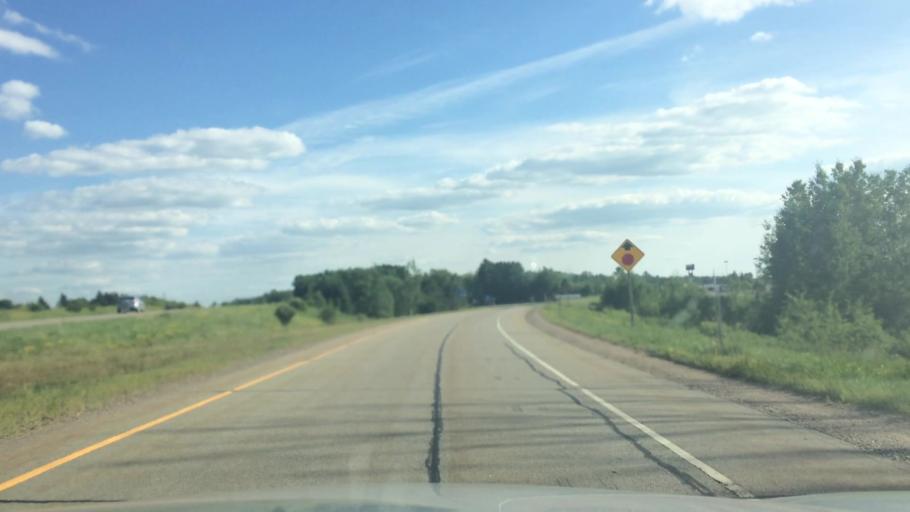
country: US
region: Wisconsin
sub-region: Lincoln County
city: Merrill
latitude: 45.1813
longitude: -89.6469
